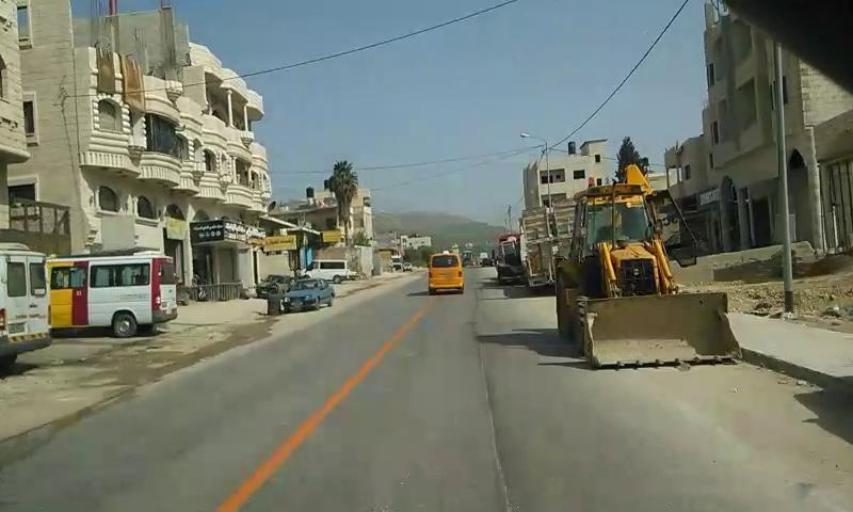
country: PS
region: West Bank
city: Huwwarah
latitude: 32.1587
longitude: 35.2604
